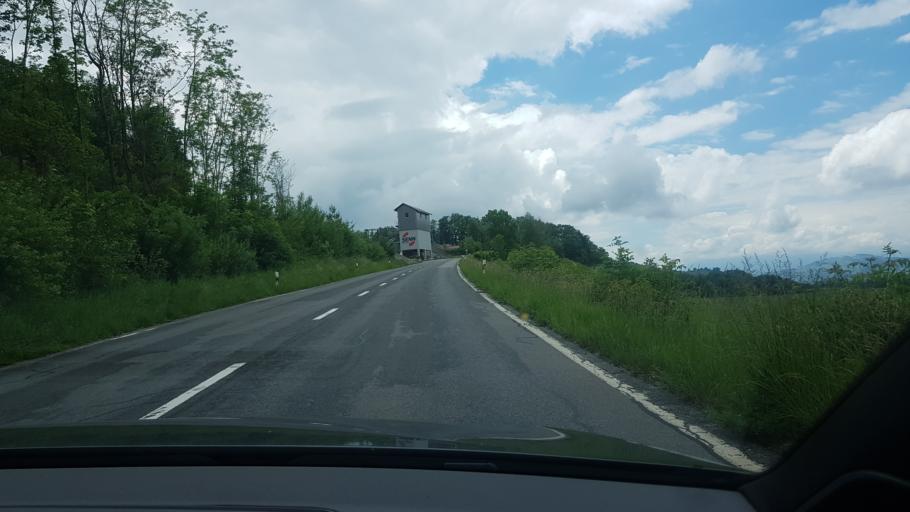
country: CH
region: Zug
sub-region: Zug
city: Menzingen
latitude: 47.1923
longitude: 8.5708
